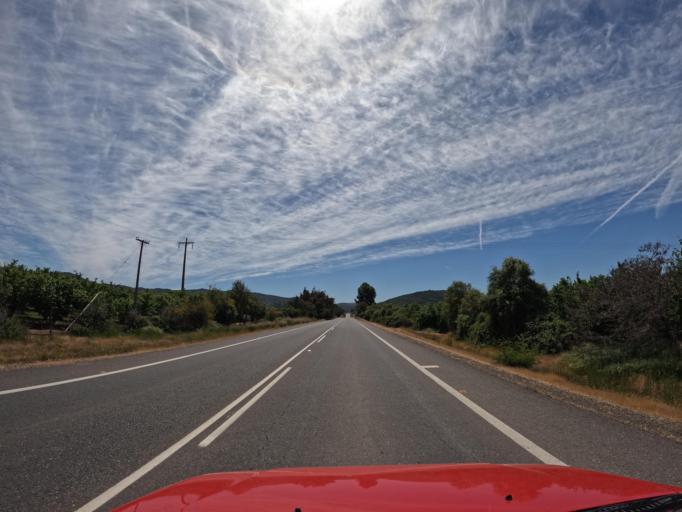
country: CL
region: Maule
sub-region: Provincia de Talca
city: Talca
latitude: -35.2756
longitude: -71.5386
